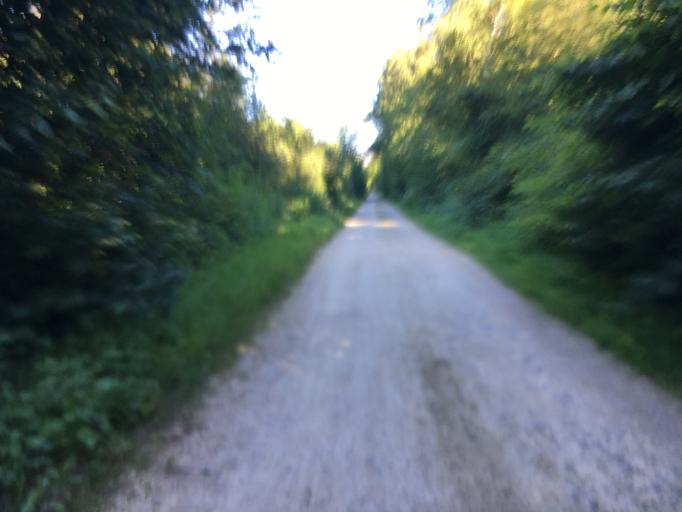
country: CH
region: Fribourg
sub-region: See District
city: Bas-Vully
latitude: 46.9503
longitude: 7.1317
